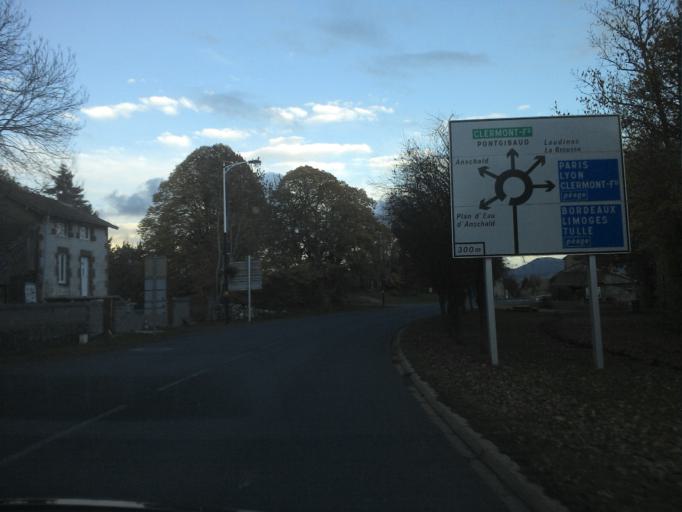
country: FR
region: Auvergne
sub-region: Departement du Puy-de-Dome
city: Chapdes-Beaufort
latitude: 45.8375
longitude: 2.8211
